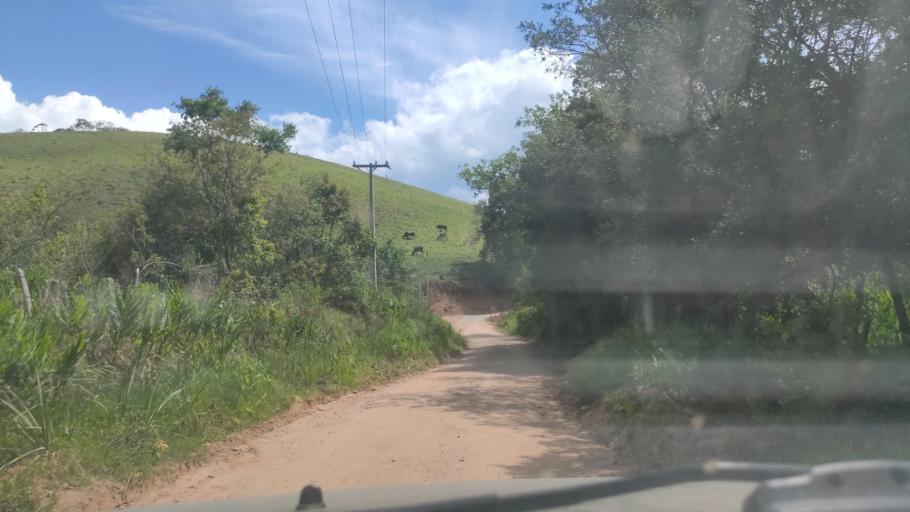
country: BR
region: Minas Gerais
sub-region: Cambui
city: Cambui
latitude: -22.7128
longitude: -46.0359
